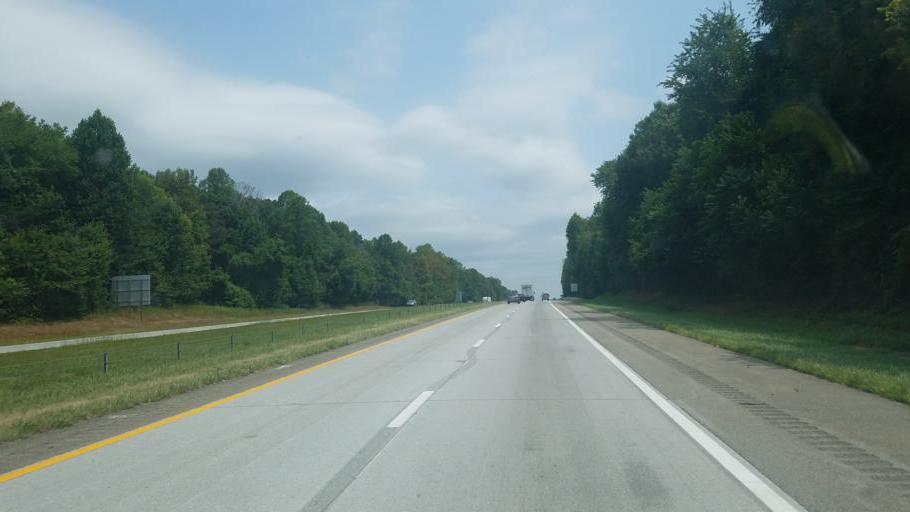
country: US
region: North Carolina
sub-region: Surry County
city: Elkin
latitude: 36.2949
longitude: -80.8131
